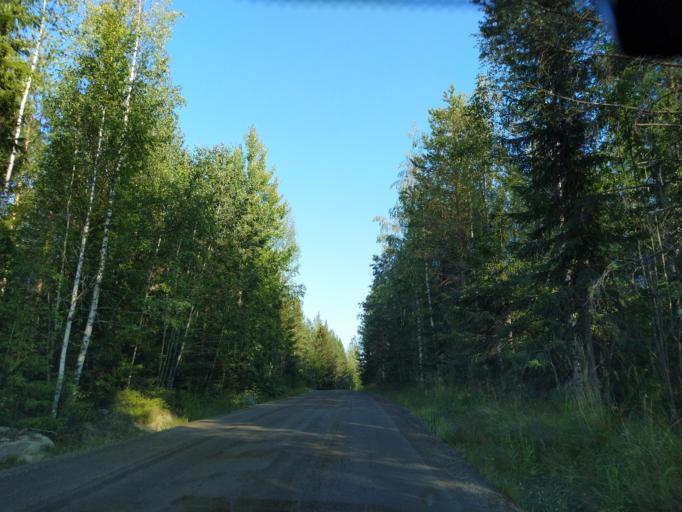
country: FI
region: Central Finland
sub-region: Jaemsae
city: Kuhmoinen
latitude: 61.6098
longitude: 25.1253
